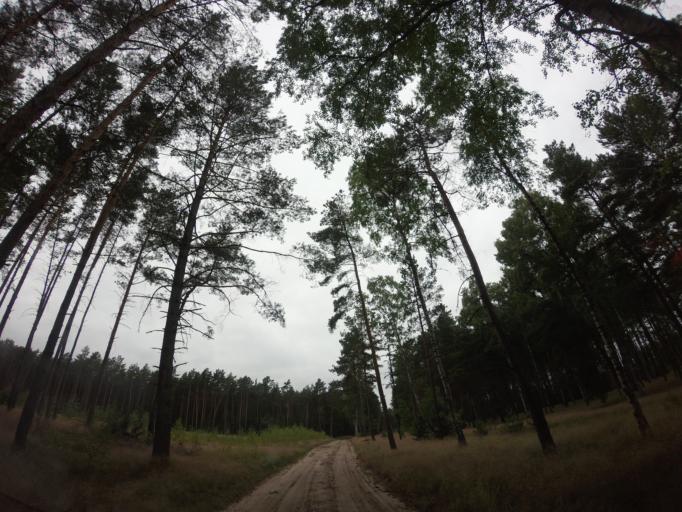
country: PL
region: West Pomeranian Voivodeship
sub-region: Powiat choszczenski
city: Drawno
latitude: 53.1421
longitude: 15.7200
